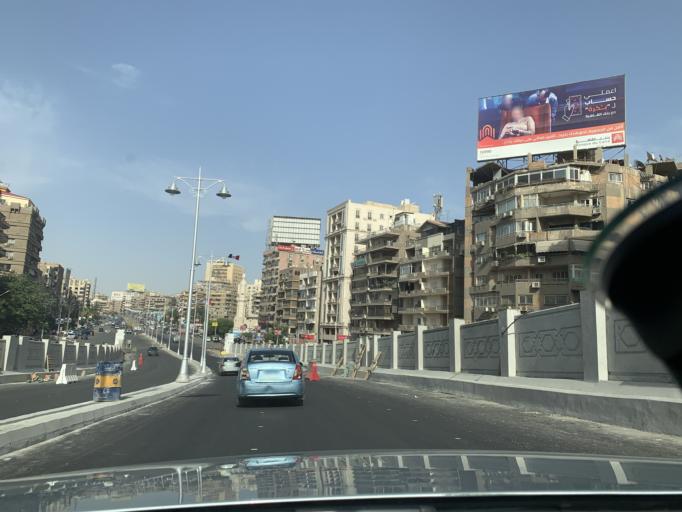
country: EG
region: Muhafazat al Qahirah
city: Cairo
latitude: 30.0843
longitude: 31.3259
